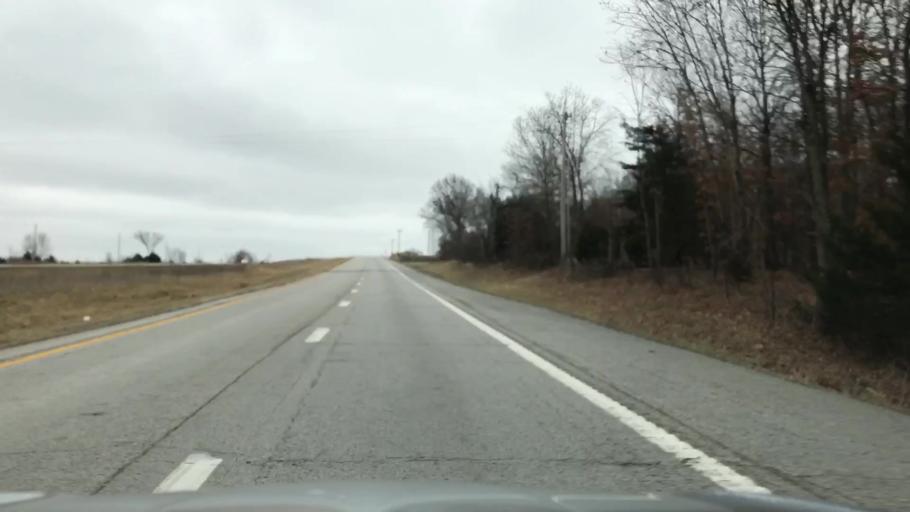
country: US
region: Missouri
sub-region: Linn County
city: Linneus
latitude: 39.7780
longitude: -93.2048
